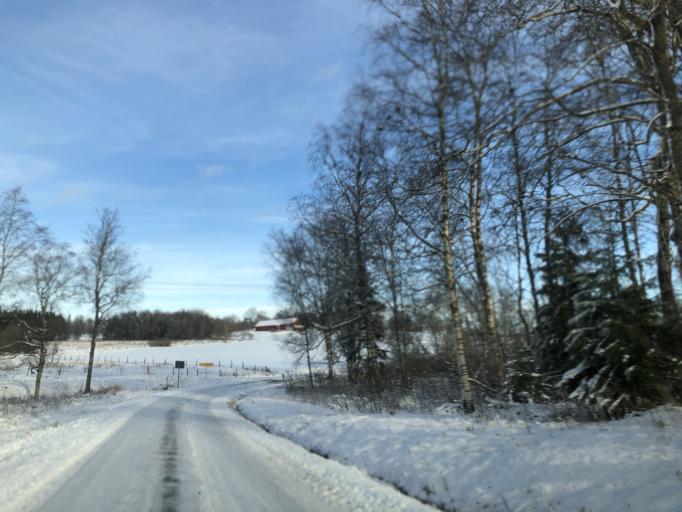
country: SE
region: Vaestra Goetaland
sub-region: Ulricehamns Kommun
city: Ulricehamn
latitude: 57.7279
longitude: 13.4704
